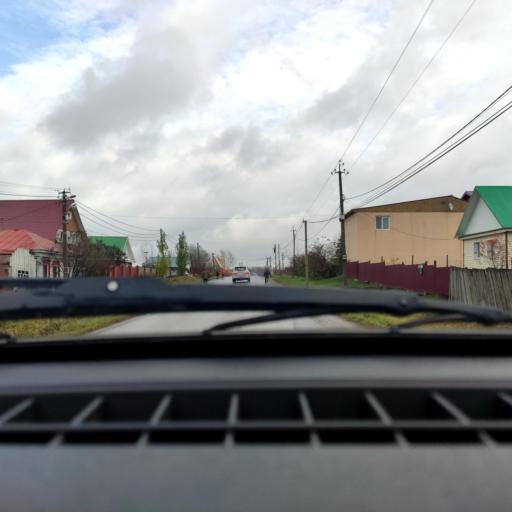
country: RU
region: Bashkortostan
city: Kabakovo
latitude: 54.6378
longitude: 56.0810
